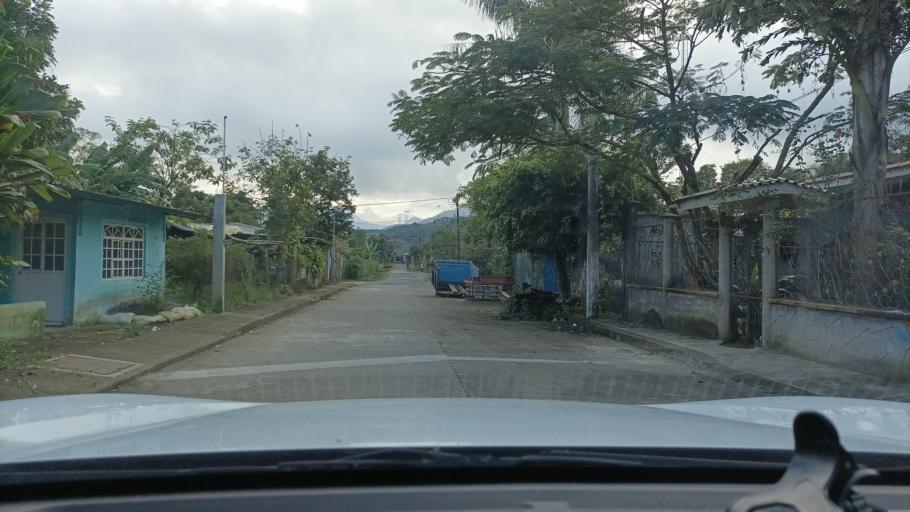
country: MX
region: Veracruz
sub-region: Ixtaczoquitlan
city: Buenavista
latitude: 18.9119
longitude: -97.0567
